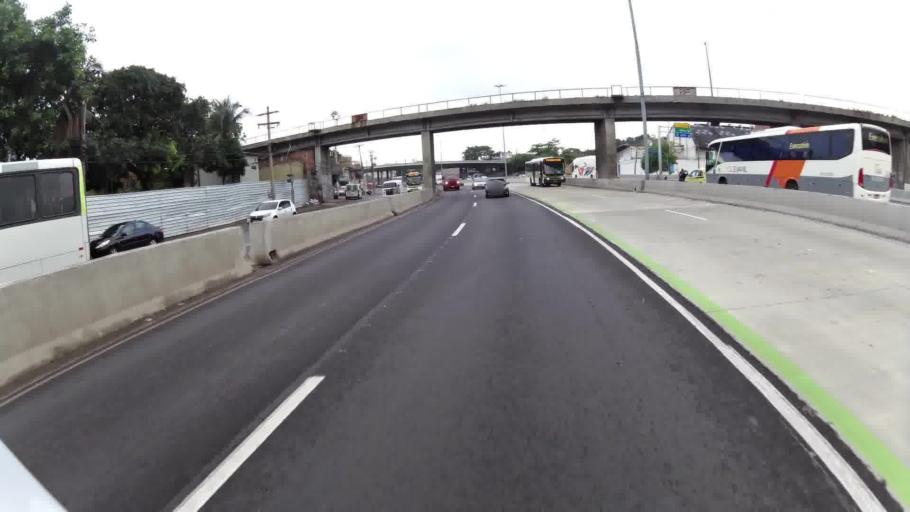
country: BR
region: Rio de Janeiro
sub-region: Rio De Janeiro
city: Rio de Janeiro
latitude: -22.8864
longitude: -43.2341
